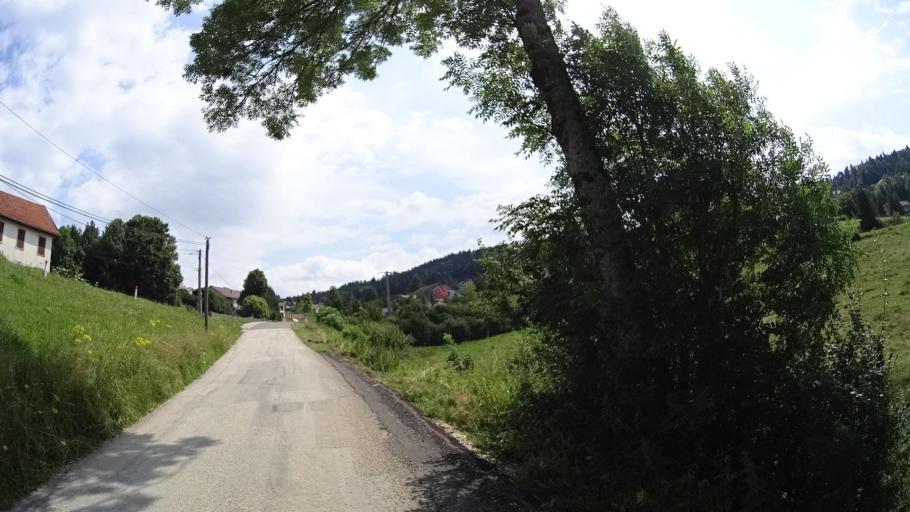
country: FR
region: Franche-Comte
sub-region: Departement du Doubs
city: Les Fourgs
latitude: 46.8361
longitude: 6.3439
